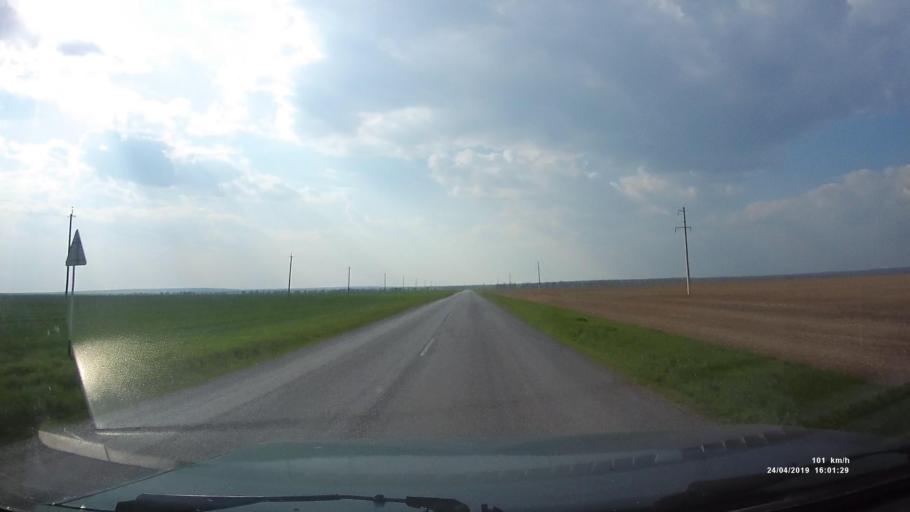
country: RU
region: Rostov
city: Sovetskoye
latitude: 46.6423
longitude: 42.4349
